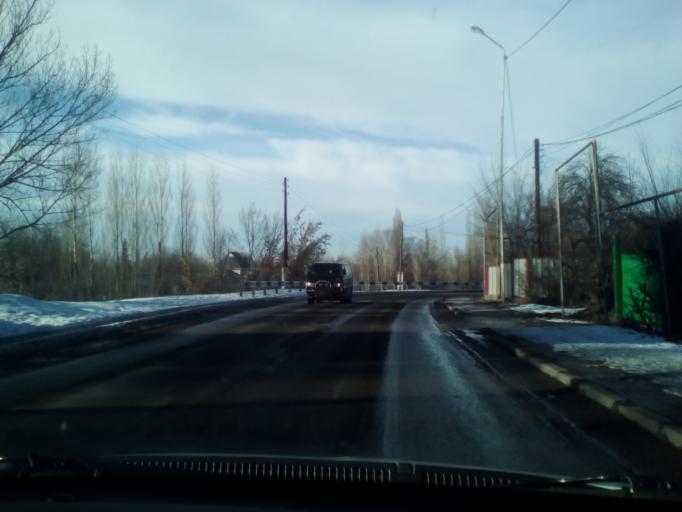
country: KZ
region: Almaty Oblysy
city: Burunday
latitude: 43.1597
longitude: 76.4174
